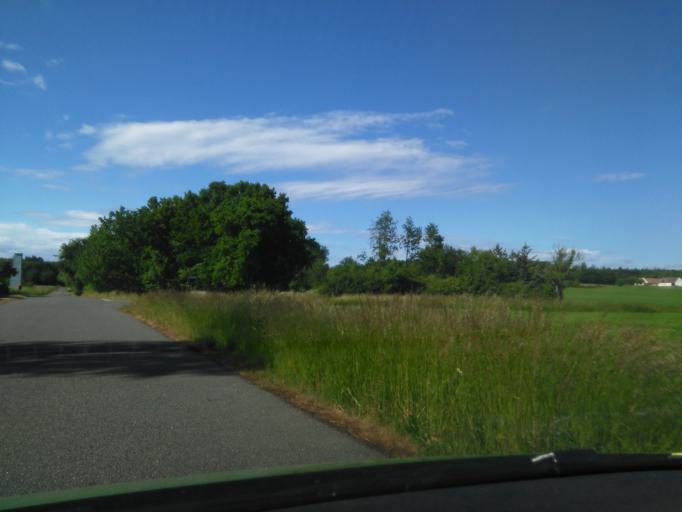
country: DK
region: Capital Region
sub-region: Bornholm Kommune
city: Nexo
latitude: 55.0775
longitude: 15.0797
